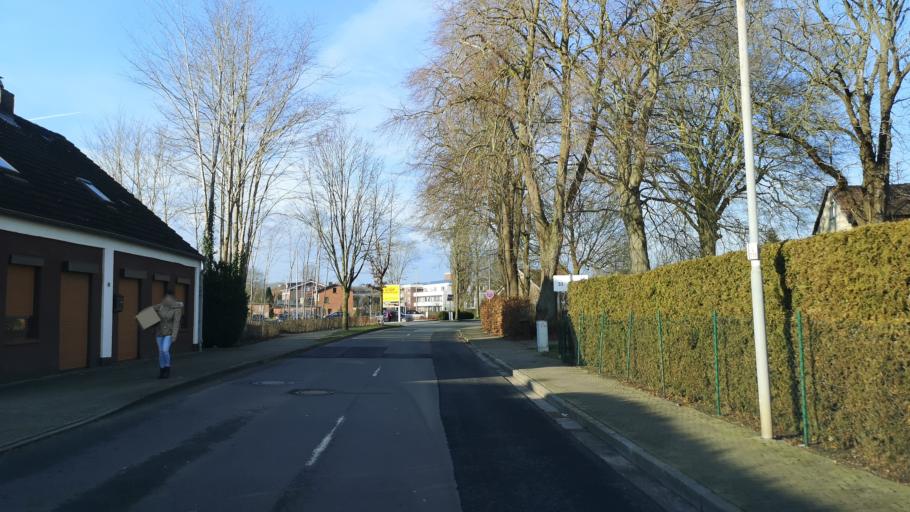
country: DE
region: Schleswig-Holstein
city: Lagerdorf
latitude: 53.8858
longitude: 9.5779
